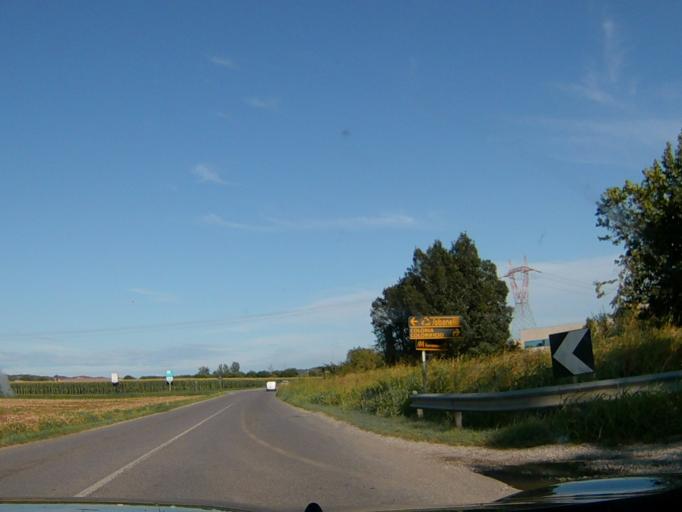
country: IT
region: Lombardy
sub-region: Provincia di Brescia
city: Ponte San Marco
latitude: 45.4736
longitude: 10.4276
